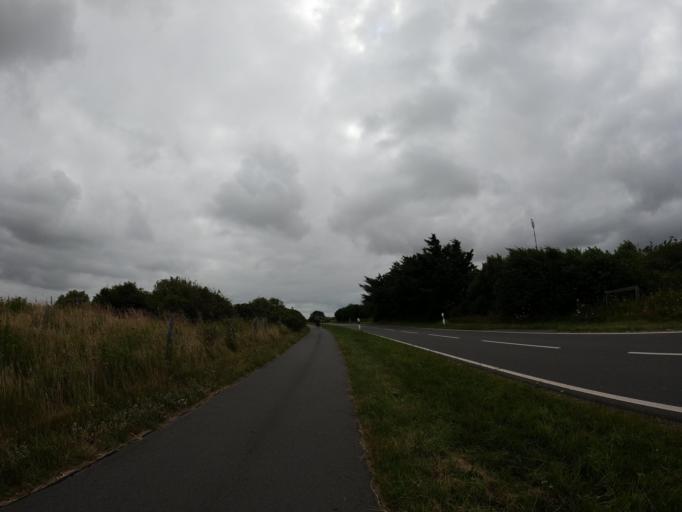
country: DE
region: Schleswig-Holstein
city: Tinnum
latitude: 54.9452
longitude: 8.3475
